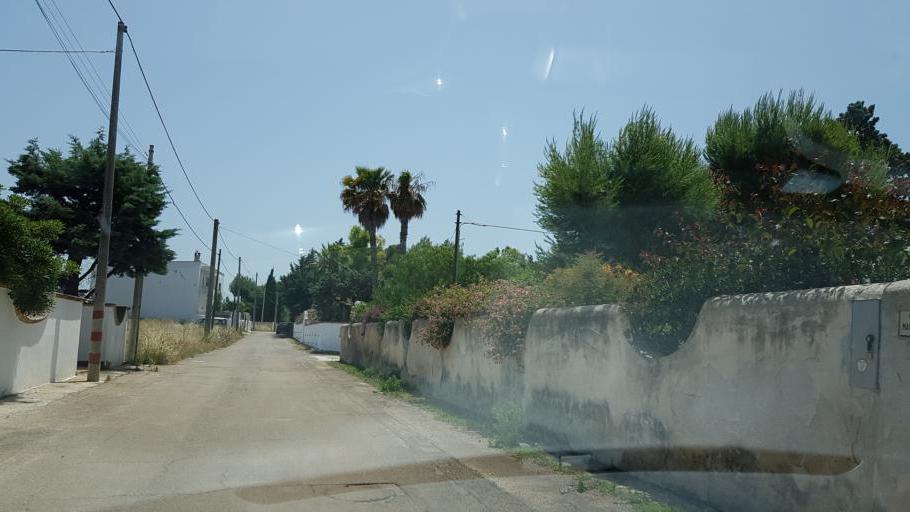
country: IT
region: Apulia
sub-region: Provincia di Lecce
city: Porto Cesareo
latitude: 40.2527
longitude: 17.9197
